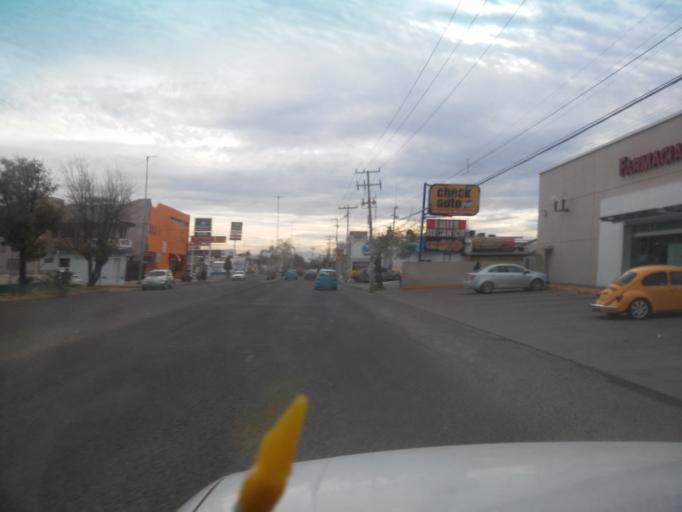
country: MX
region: Durango
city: Victoria de Durango
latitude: 24.0111
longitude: -104.6686
